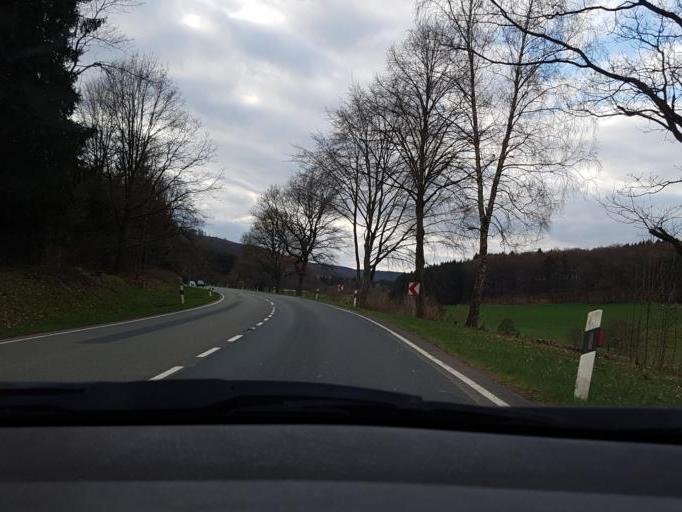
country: DE
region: Lower Saxony
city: Bodenfelde
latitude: 51.7086
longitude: 9.5443
